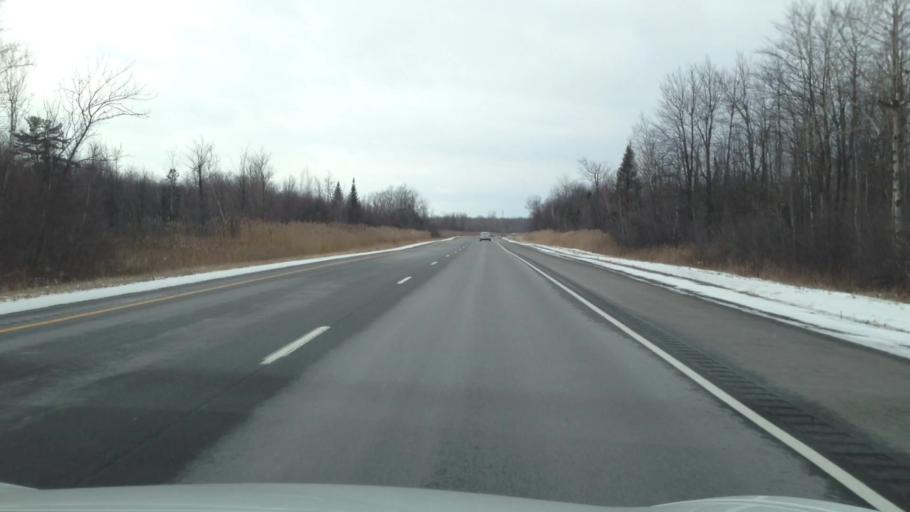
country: CA
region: Ontario
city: Bourget
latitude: 45.3306
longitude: -75.2947
